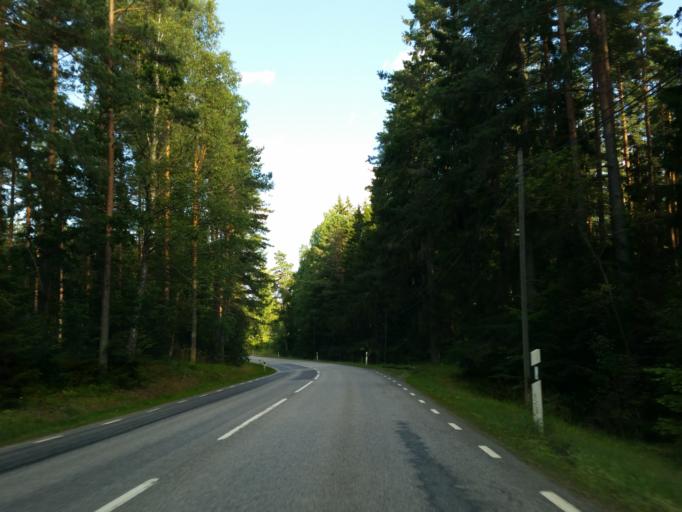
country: SE
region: Stockholm
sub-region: Nykvarns Kommun
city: Nykvarn
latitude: 59.2065
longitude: 17.3866
